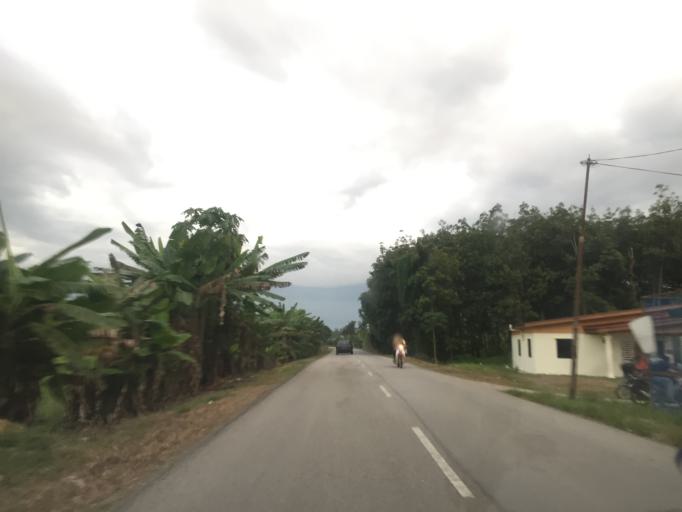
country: MY
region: Penang
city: Tasek Glugor
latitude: 5.5362
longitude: 100.5168
